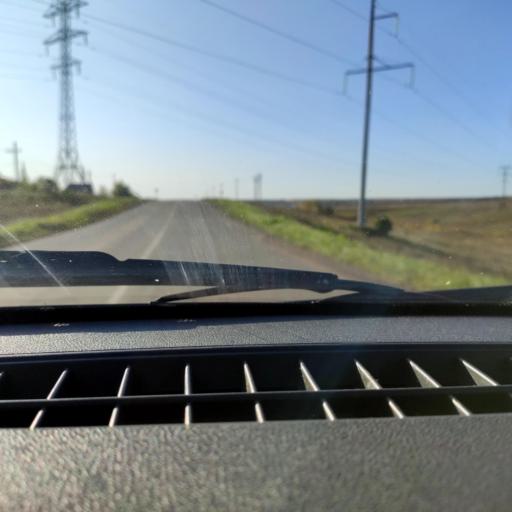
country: RU
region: Bashkortostan
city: Avdon
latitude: 54.5712
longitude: 55.7561
